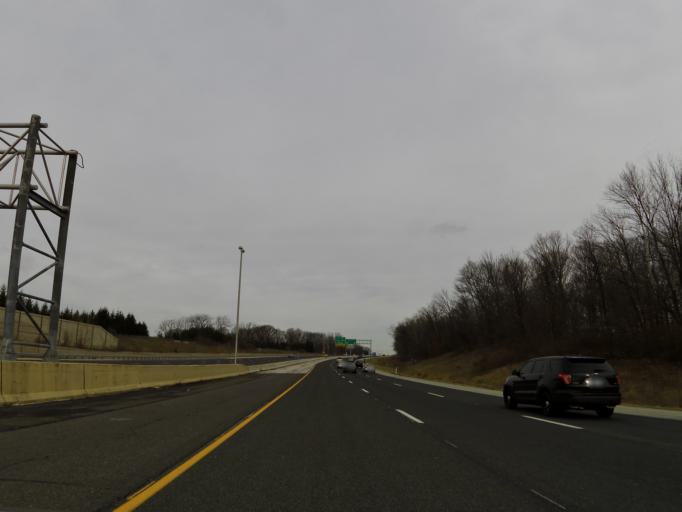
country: US
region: Indiana
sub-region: Boone County
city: Zionsville
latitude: 39.9170
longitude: -86.2696
